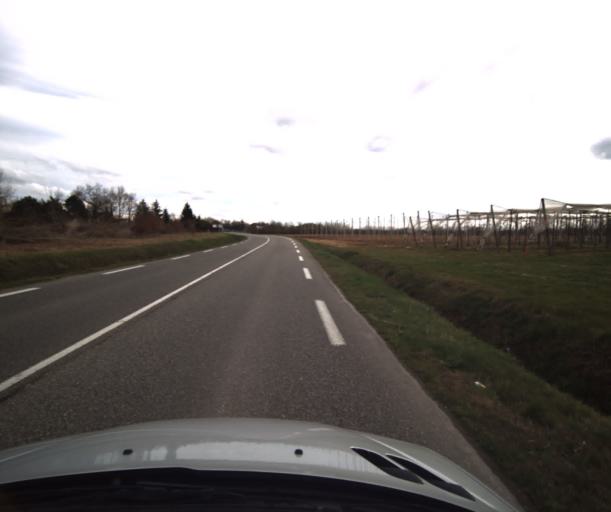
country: FR
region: Midi-Pyrenees
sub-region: Departement du Tarn-et-Garonne
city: Montbeton
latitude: 44.0364
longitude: 1.3108
